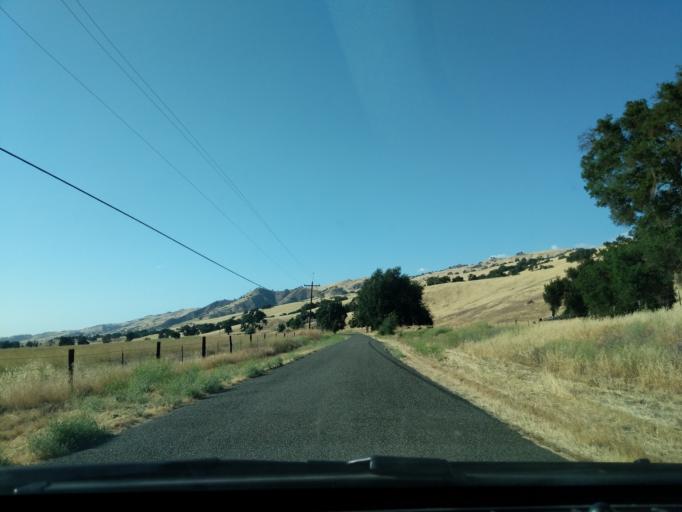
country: US
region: California
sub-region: Monterey County
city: King City
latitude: 36.1420
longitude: -120.7531
